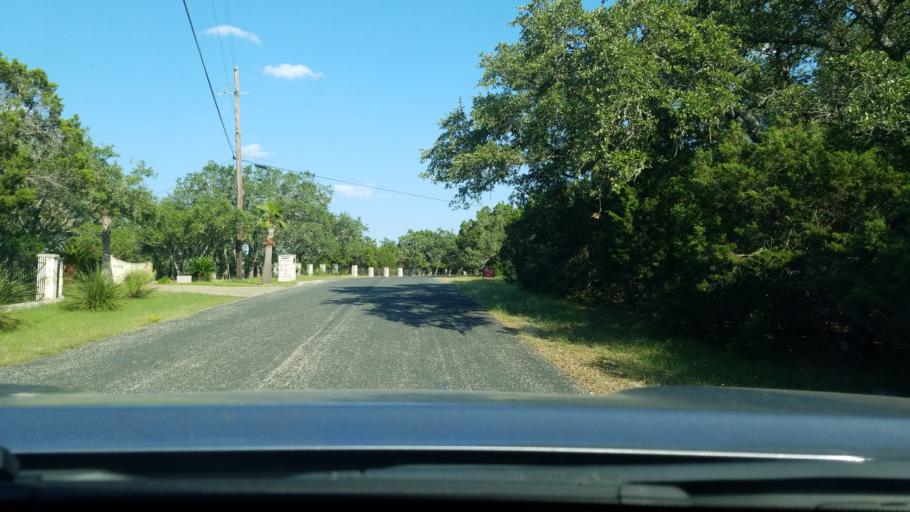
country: US
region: Texas
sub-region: Bexar County
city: Timberwood Park
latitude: 29.7079
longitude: -98.4447
